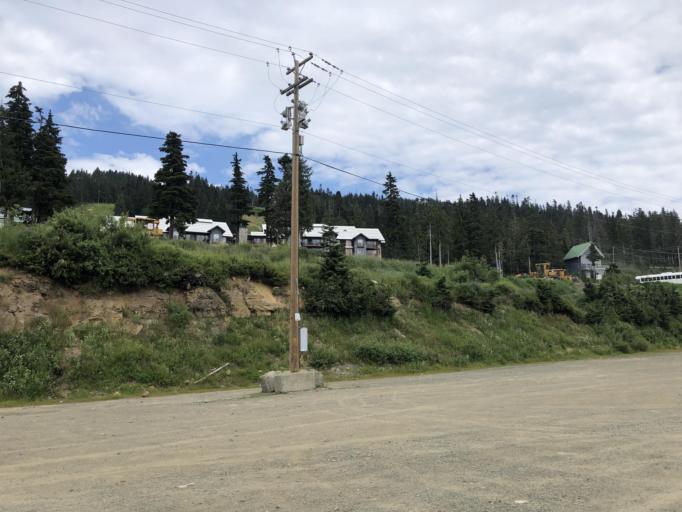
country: CA
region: British Columbia
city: Campbell River
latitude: 49.7410
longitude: -125.3010
